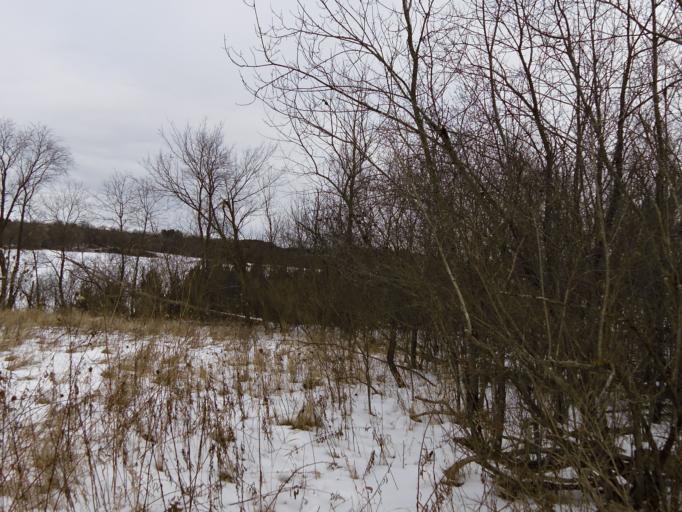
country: US
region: Wisconsin
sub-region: Pierce County
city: Prescott
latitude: 44.8024
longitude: -92.8169
